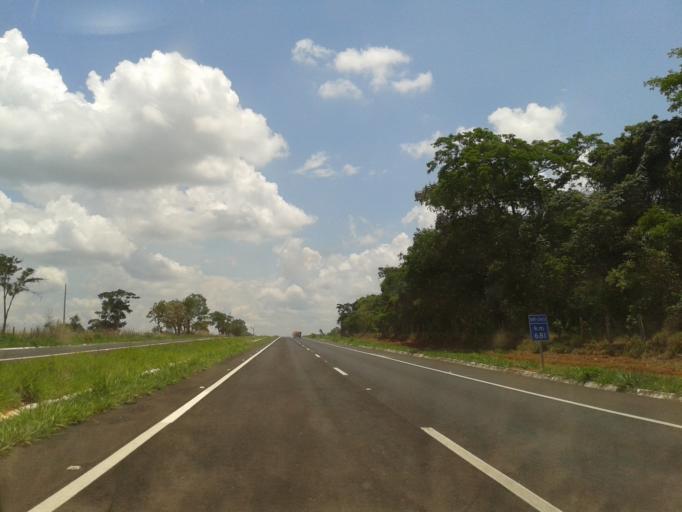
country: BR
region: Minas Gerais
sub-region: Monte Alegre De Minas
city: Monte Alegre de Minas
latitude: -18.8505
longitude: -48.8035
